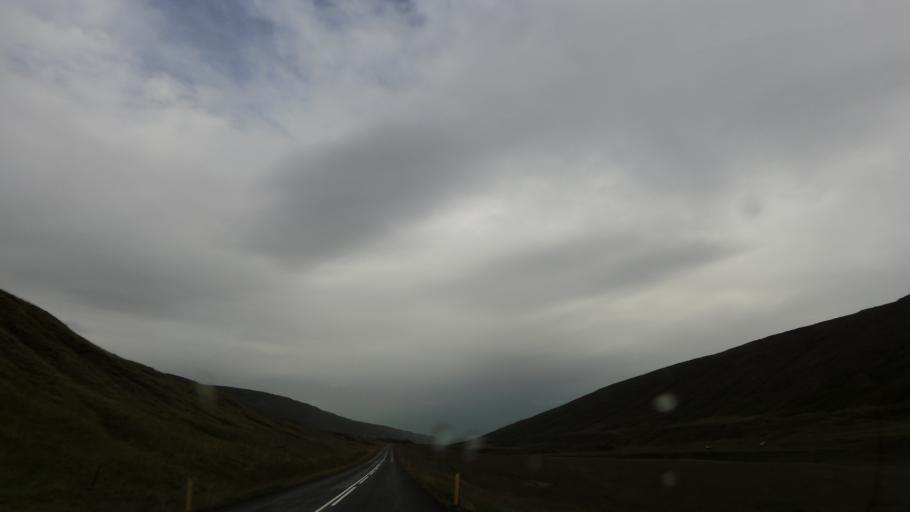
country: IS
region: East
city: Egilsstadir
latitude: 65.3200
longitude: -15.1034
